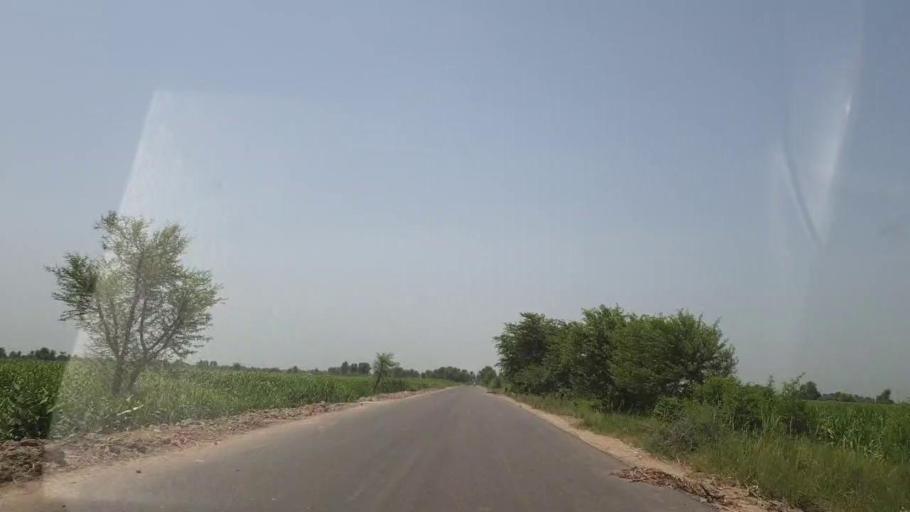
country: PK
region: Sindh
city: Ranipur
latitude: 27.2966
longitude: 68.6050
